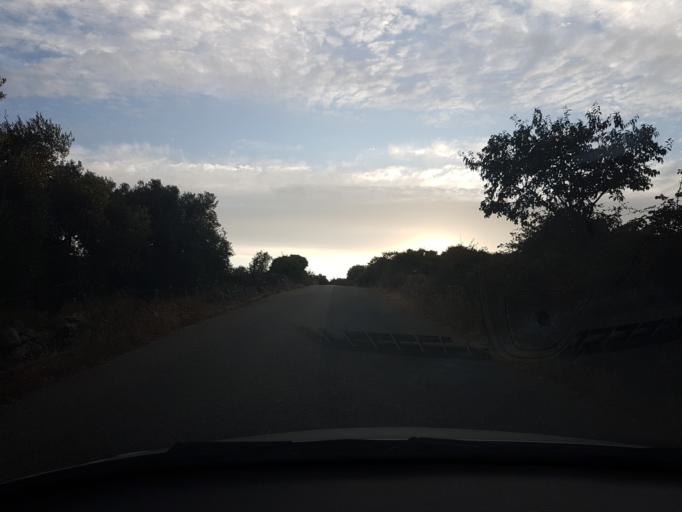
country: IT
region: Sardinia
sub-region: Provincia di Oristano
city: Seneghe
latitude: 40.0985
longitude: 8.6244
